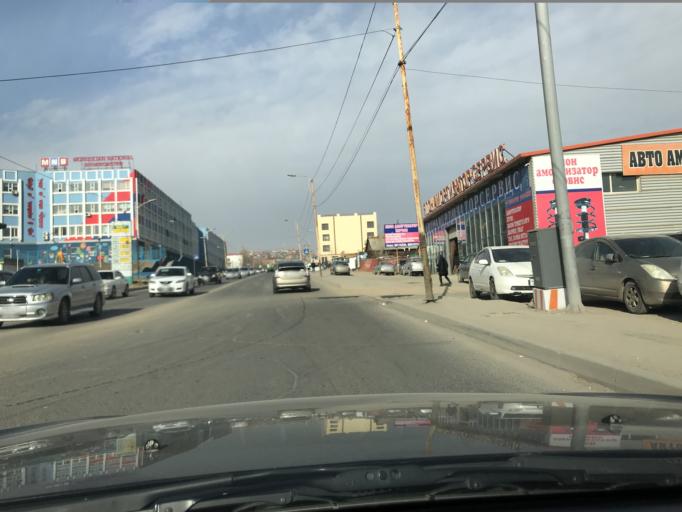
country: MN
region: Ulaanbaatar
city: Ulaanbaatar
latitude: 47.9281
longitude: 106.8919
